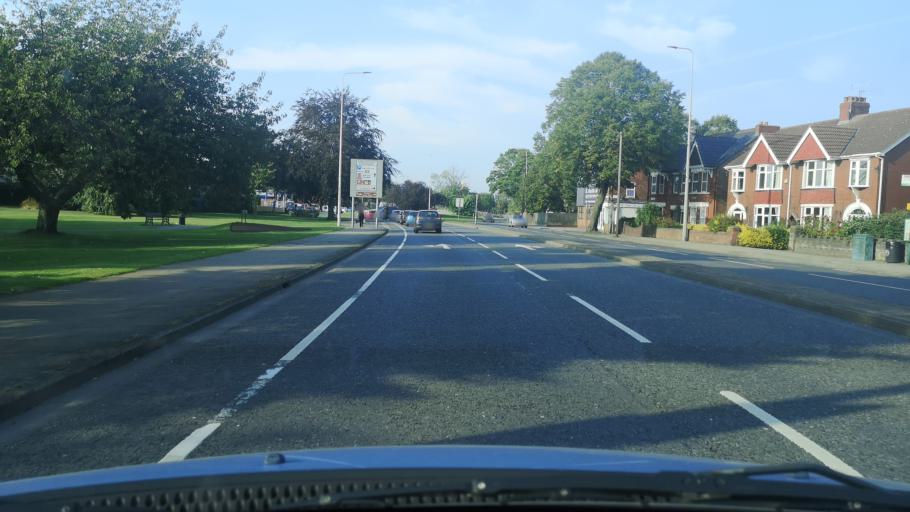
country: GB
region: England
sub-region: North Lincolnshire
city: Scunthorpe
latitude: 53.5831
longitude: -0.6535
